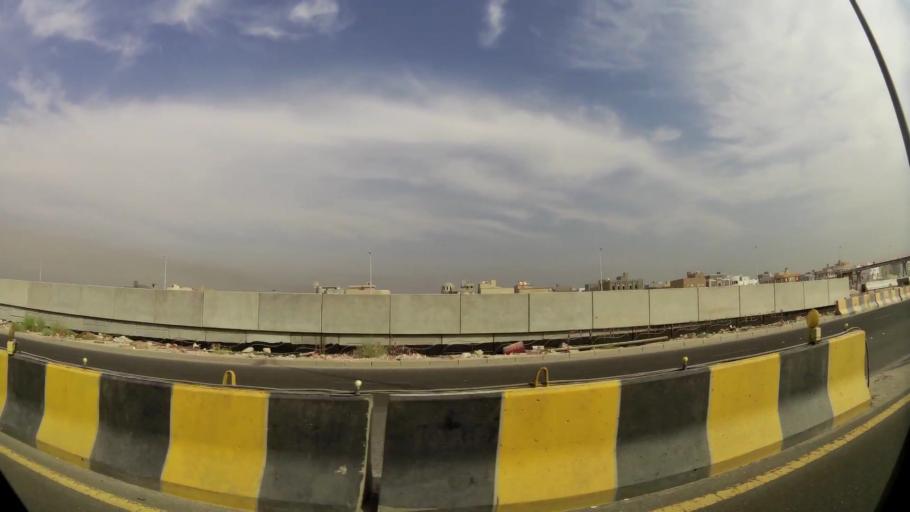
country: KW
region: Al Asimah
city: Ar Rabiyah
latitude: 29.3200
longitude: 47.8077
